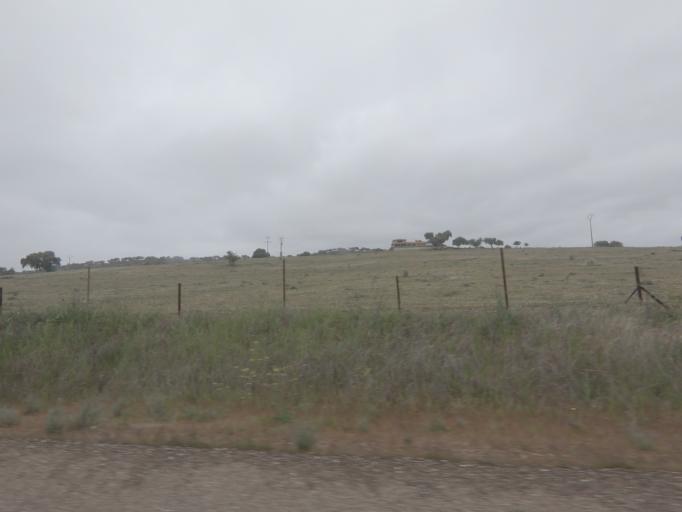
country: ES
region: Extremadura
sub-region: Provincia de Badajoz
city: La Roca de la Sierra
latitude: 39.1084
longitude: -6.7061
